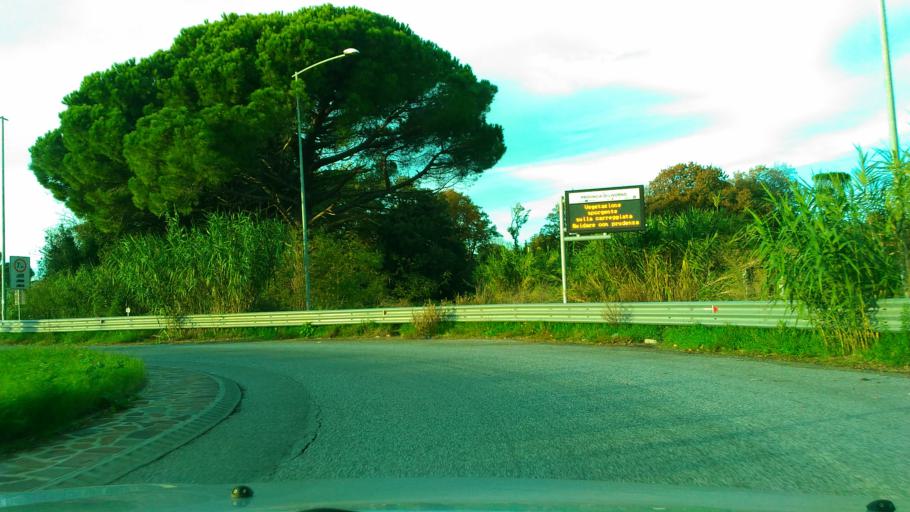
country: IT
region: Tuscany
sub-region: Provincia di Livorno
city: S.P. in Palazzi
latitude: 43.3729
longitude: 10.5046
